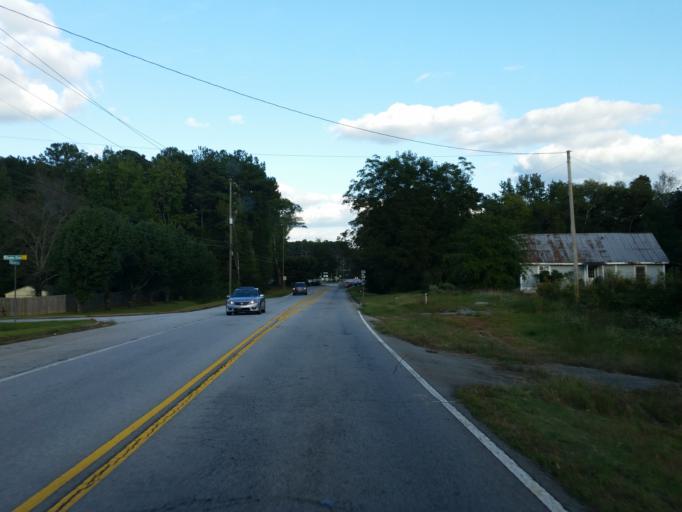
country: US
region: Georgia
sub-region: Paulding County
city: Hiram
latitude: 33.9087
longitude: -84.7517
